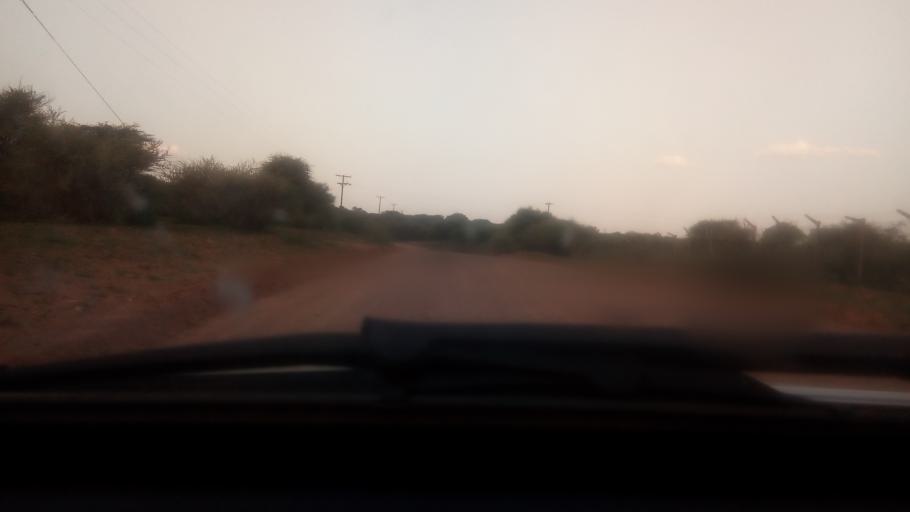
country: BW
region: Kgatleng
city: Bokaa
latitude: -24.4321
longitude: 26.0049
